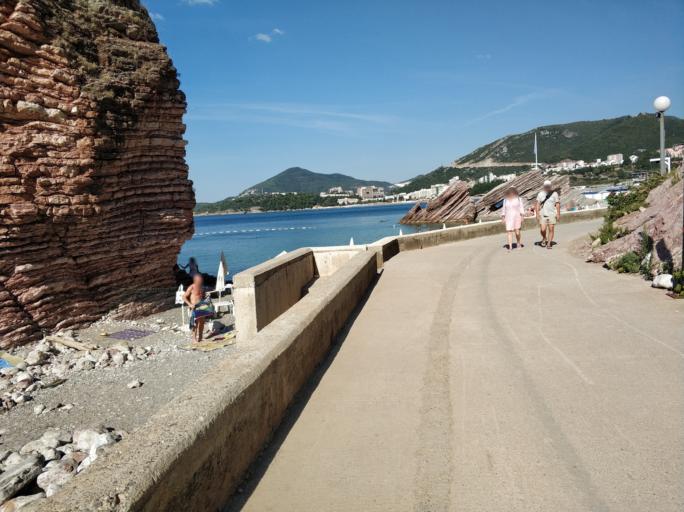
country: ME
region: Budva
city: Budva
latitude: 42.2768
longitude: 18.8817
